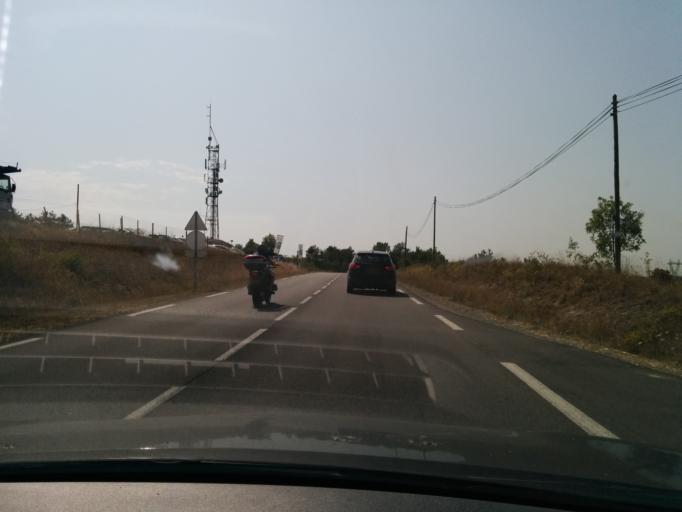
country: FR
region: Midi-Pyrenees
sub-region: Departement du Tarn
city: Castelnau-de-Levis
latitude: 43.9573
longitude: 2.1124
